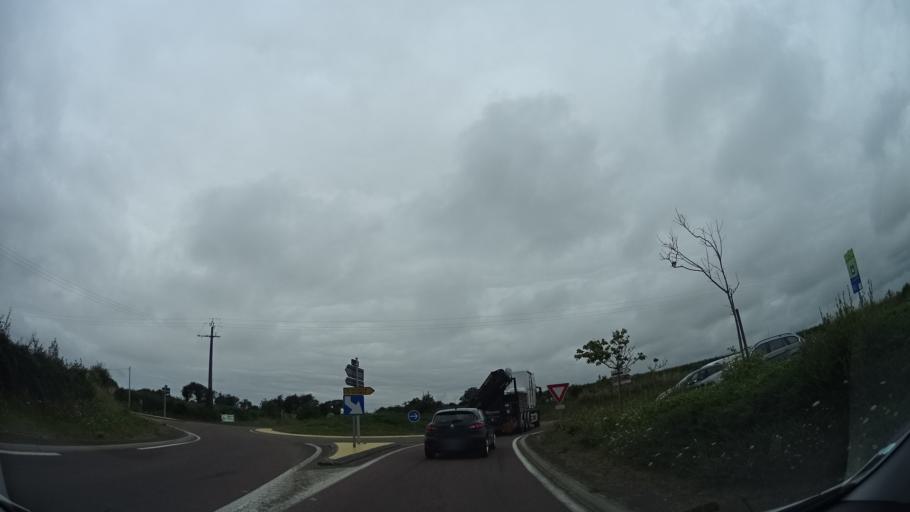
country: FR
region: Lower Normandy
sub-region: Departement de la Manche
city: Portbail
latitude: 49.3615
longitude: -1.6954
